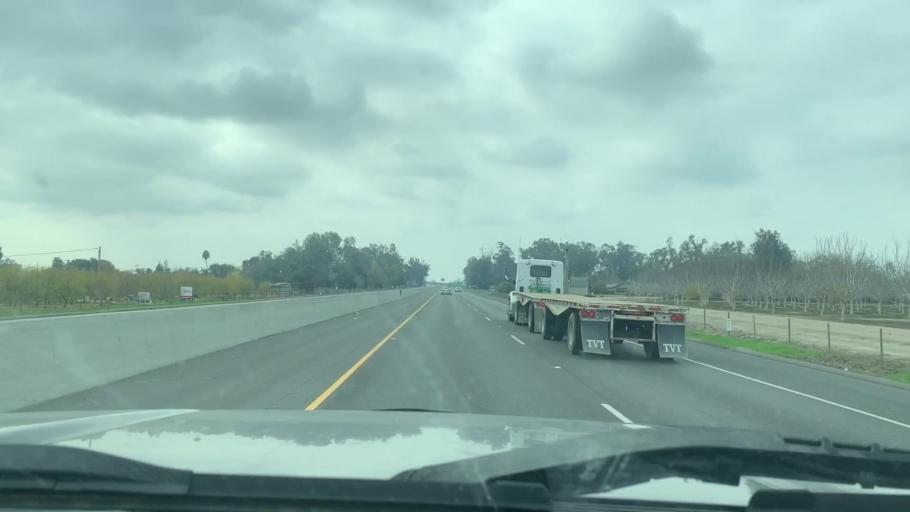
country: US
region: California
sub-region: Kings County
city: Armona
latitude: 36.3015
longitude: -119.7397
